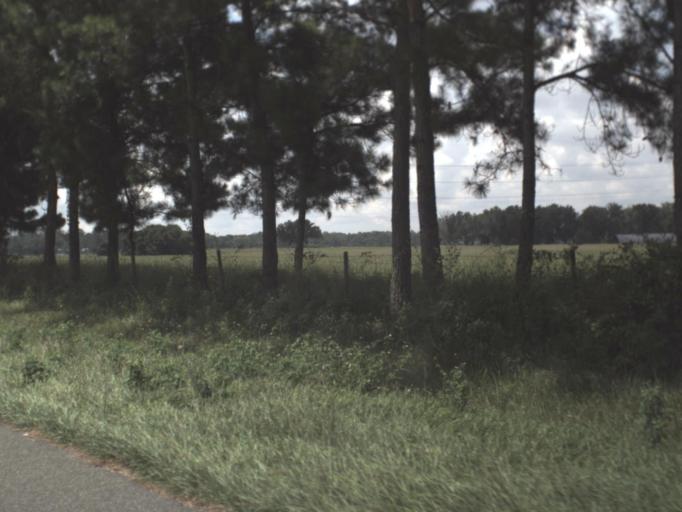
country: US
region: Florida
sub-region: Gilchrist County
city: Trenton
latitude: 29.6298
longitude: -82.8240
